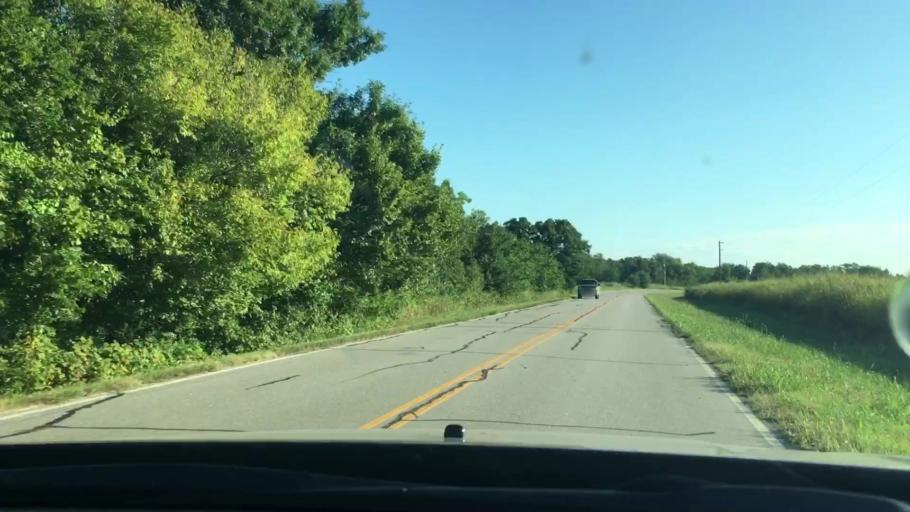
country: US
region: Oklahoma
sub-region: Pontotoc County
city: Ada
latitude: 34.6967
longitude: -96.4415
